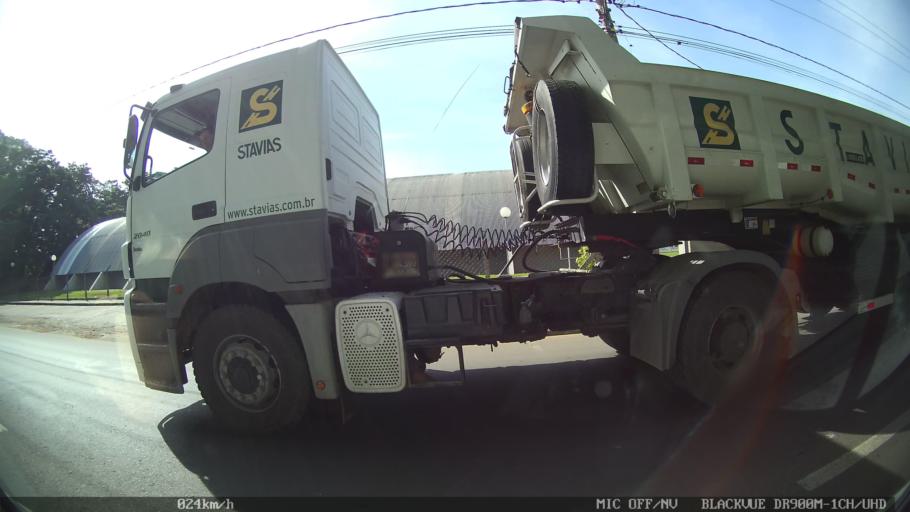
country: BR
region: Sao Paulo
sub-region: Piracicaba
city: Piracicaba
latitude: -22.7400
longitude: -47.6690
